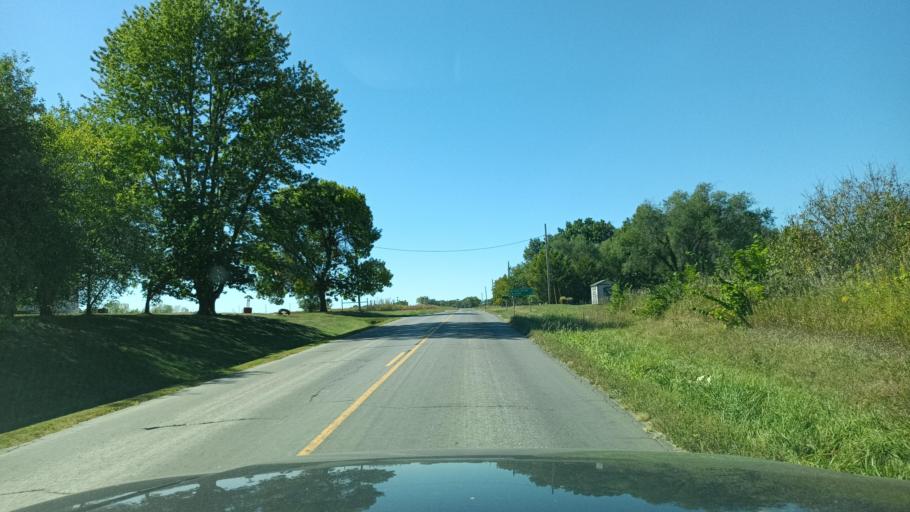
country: US
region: Missouri
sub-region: Macon County
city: La Plata
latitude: 40.0234
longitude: -92.5978
